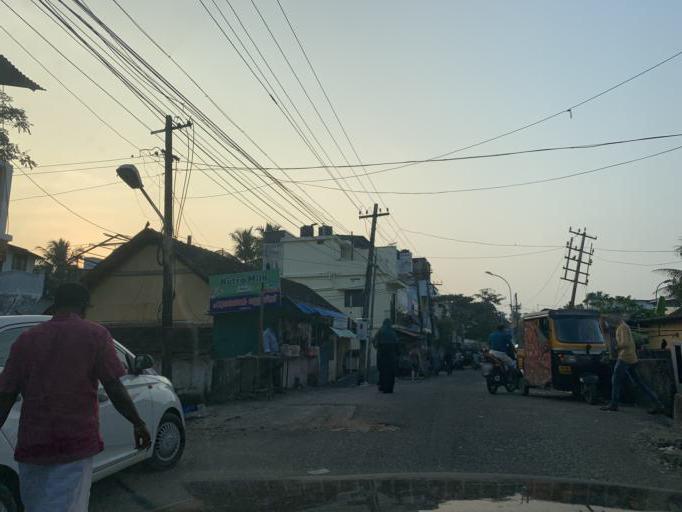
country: IN
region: Kerala
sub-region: Ernakulam
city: Cochin
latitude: 9.9632
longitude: 76.2508
